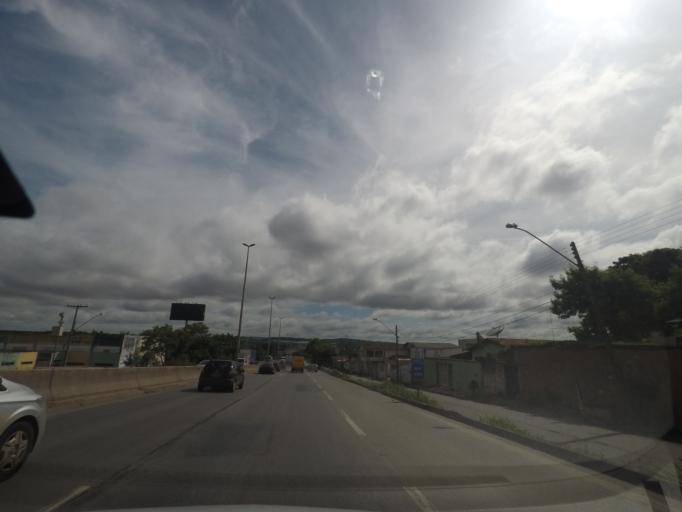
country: BR
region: Goias
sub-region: Goiania
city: Goiania
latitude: -16.6617
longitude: -49.2219
